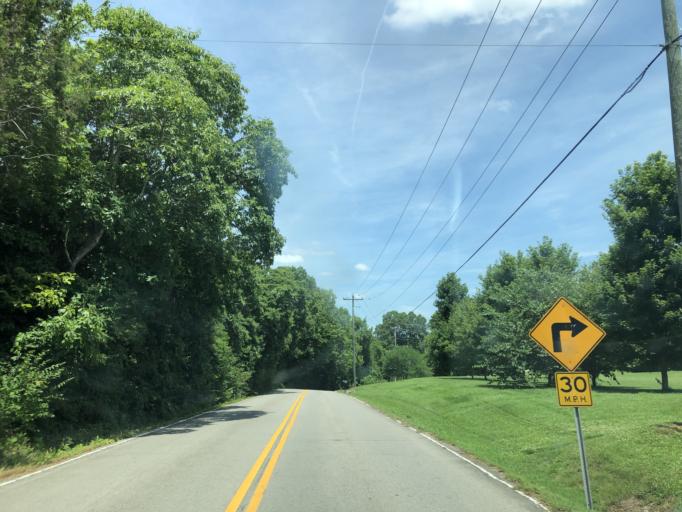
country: US
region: Tennessee
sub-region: Williamson County
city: Nolensville
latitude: 36.0329
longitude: -86.6613
